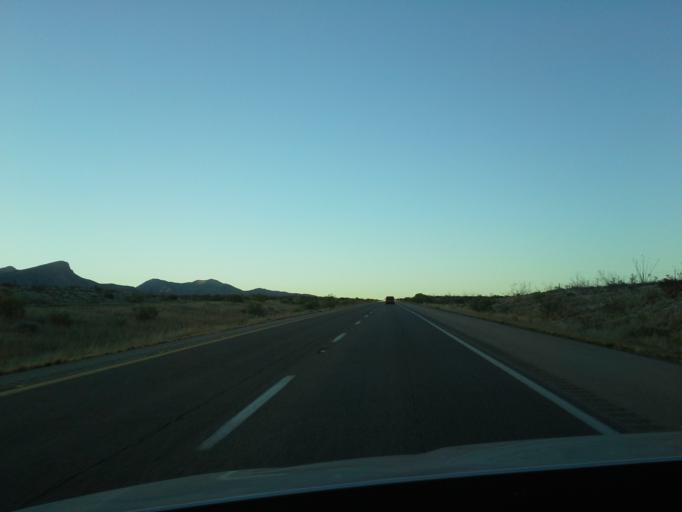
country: US
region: Arizona
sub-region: Cochise County
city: Huachuca City
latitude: 31.7587
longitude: -110.3500
